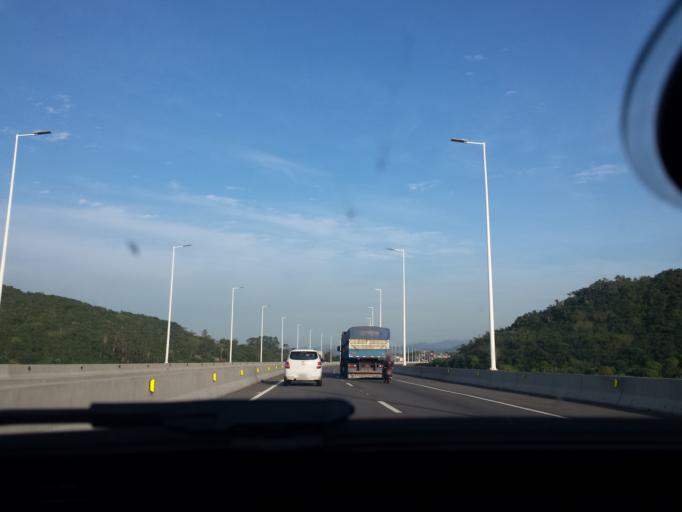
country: BR
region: Santa Catarina
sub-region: Laguna
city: Laguna
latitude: -28.4336
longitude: -48.8453
